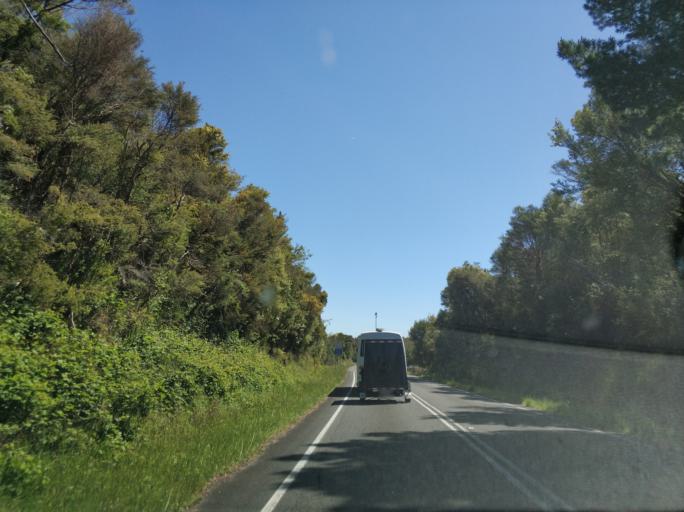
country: AU
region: Victoria
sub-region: Colac-Otway
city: Apollo Bay
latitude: -38.7360
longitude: 143.2982
